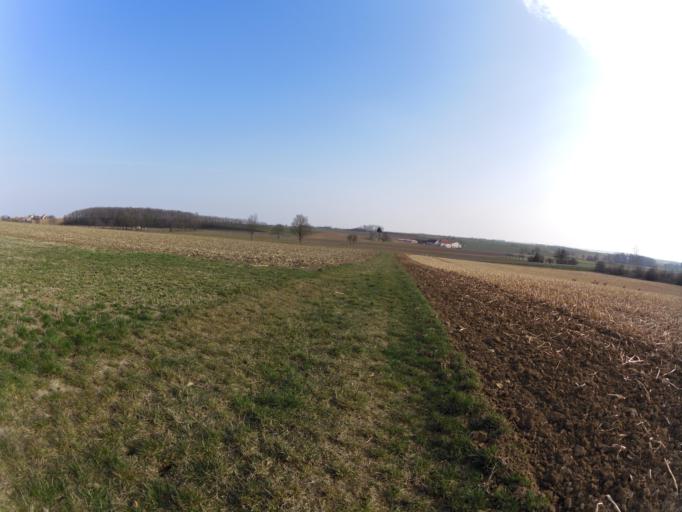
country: DE
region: Bavaria
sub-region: Regierungsbezirk Unterfranken
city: Sulzdorf
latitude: 49.6579
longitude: 9.9157
